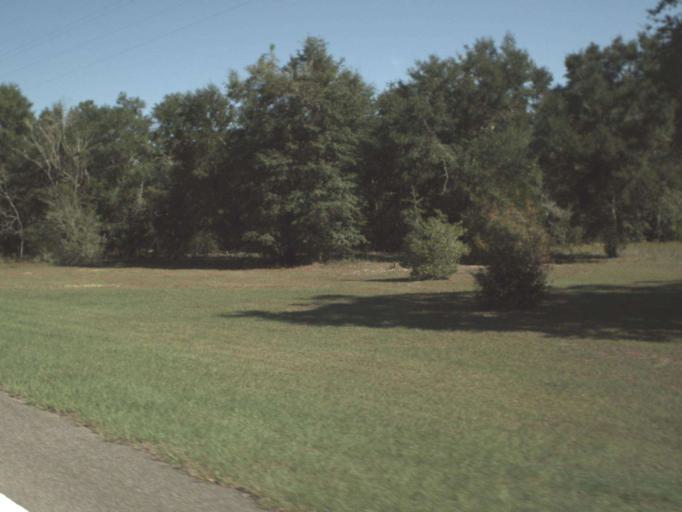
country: US
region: Florida
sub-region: Walton County
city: Freeport
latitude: 30.5650
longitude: -85.9210
